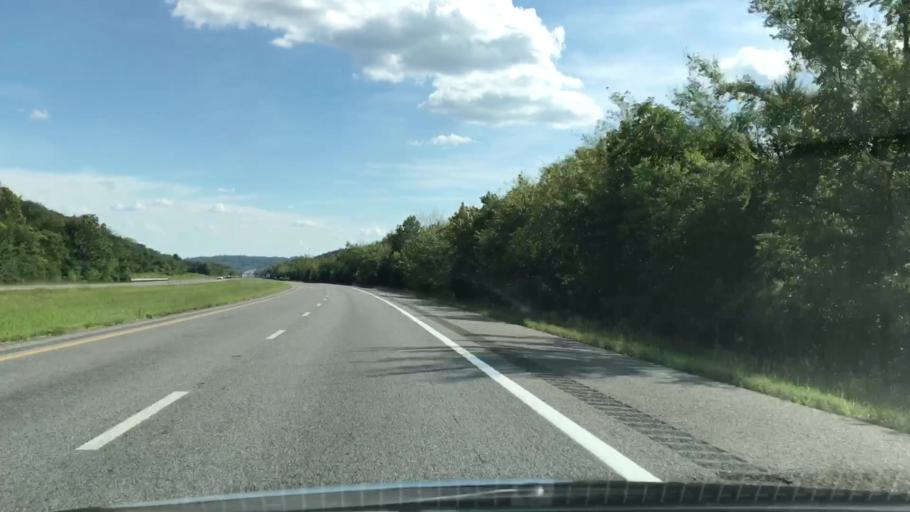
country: US
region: Tennessee
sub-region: Giles County
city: Pulaski
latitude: 35.1624
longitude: -86.8801
